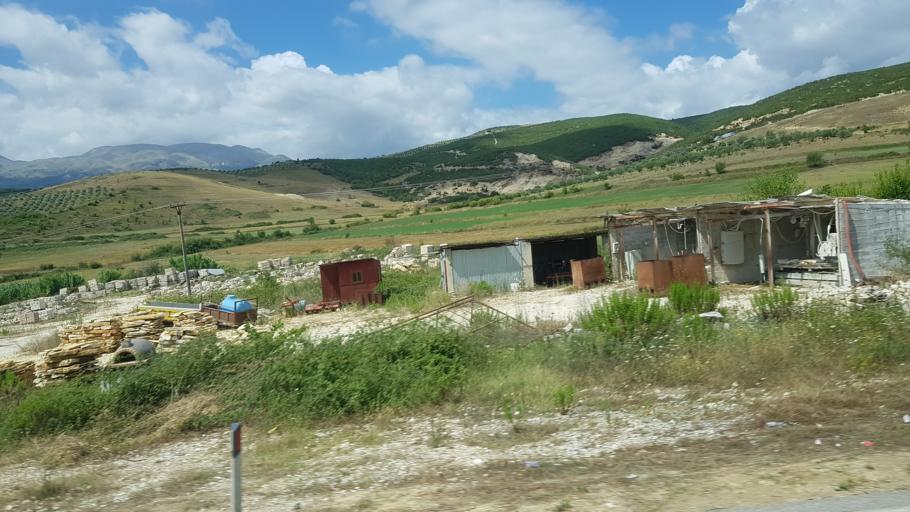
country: AL
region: Gjirokaster
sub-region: Rrethi i Tepelenes
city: Krahes
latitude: 40.4270
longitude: 19.8537
